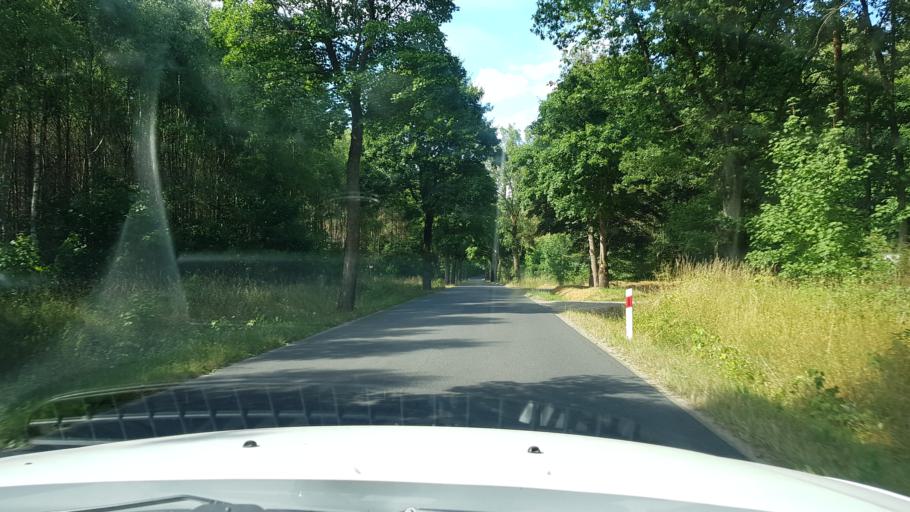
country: PL
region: West Pomeranian Voivodeship
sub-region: Powiat drawski
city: Zlocieniec
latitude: 53.5674
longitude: 16.0100
